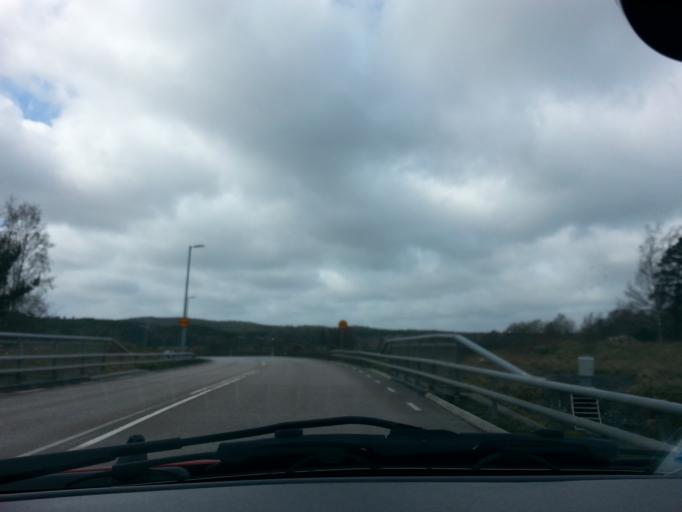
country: SE
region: Vaestra Goetaland
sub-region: Lerums Kommun
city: Stenkullen
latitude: 57.7962
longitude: 12.3073
